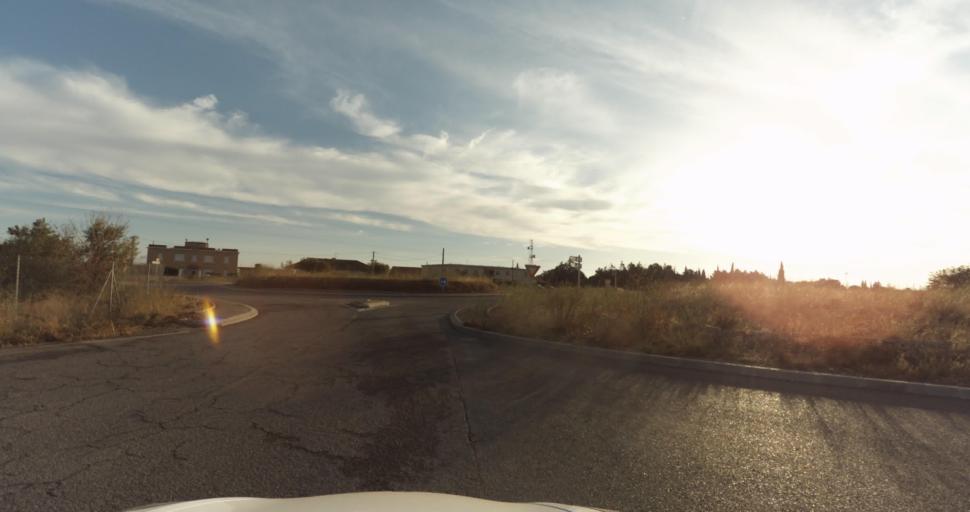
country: FR
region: Provence-Alpes-Cote d'Azur
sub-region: Departement des Bouches-du-Rhone
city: Miramas
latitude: 43.5870
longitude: 4.9814
